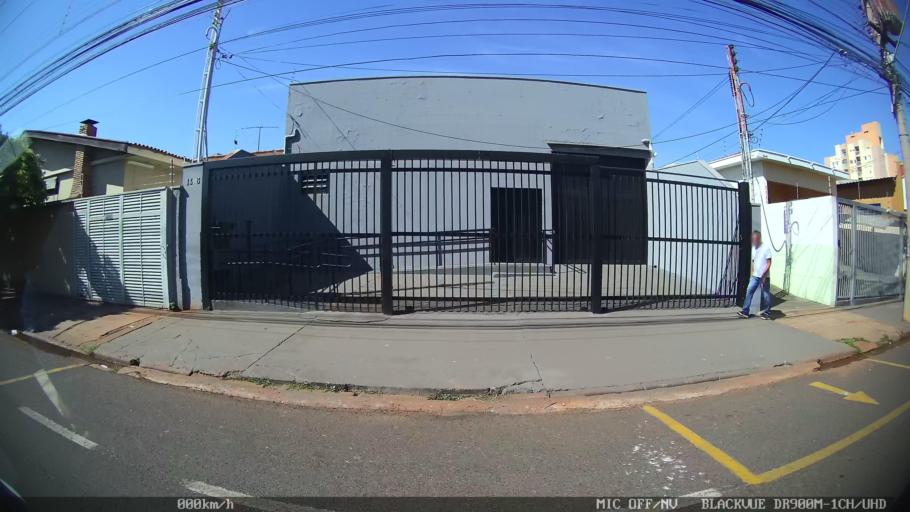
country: BR
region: Sao Paulo
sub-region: Sao Jose Do Rio Preto
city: Sao Jose do Rio Preto
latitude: -20.8015
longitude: -49.3974
